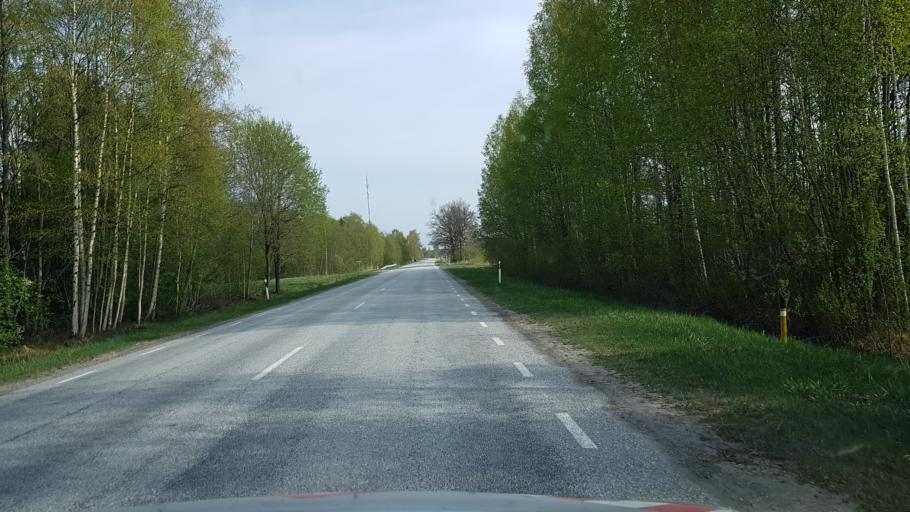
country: EE
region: Paernumaa
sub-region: Audru vald
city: Audru
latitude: 58.4091
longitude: 24.3082
